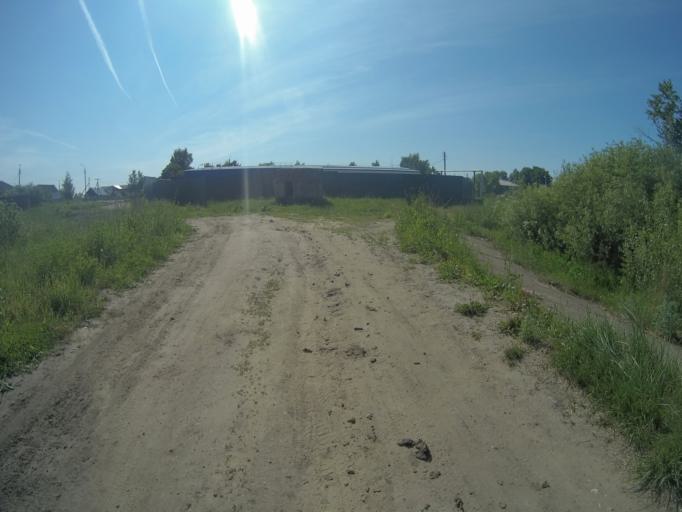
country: RU
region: Vladimir
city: Stavrovo
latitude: 56.1450
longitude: 40.0495
